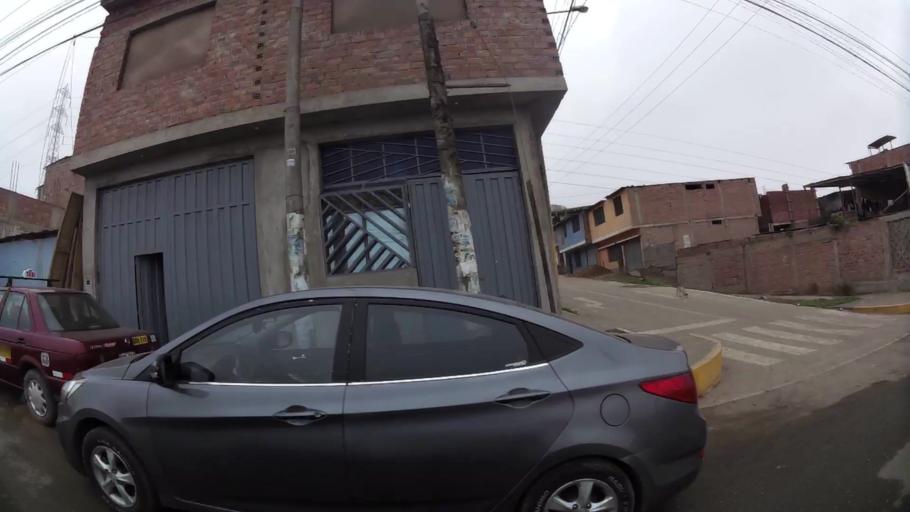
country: PE
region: Lima
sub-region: Lima
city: Surco
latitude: -12.2159
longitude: -76.9209
